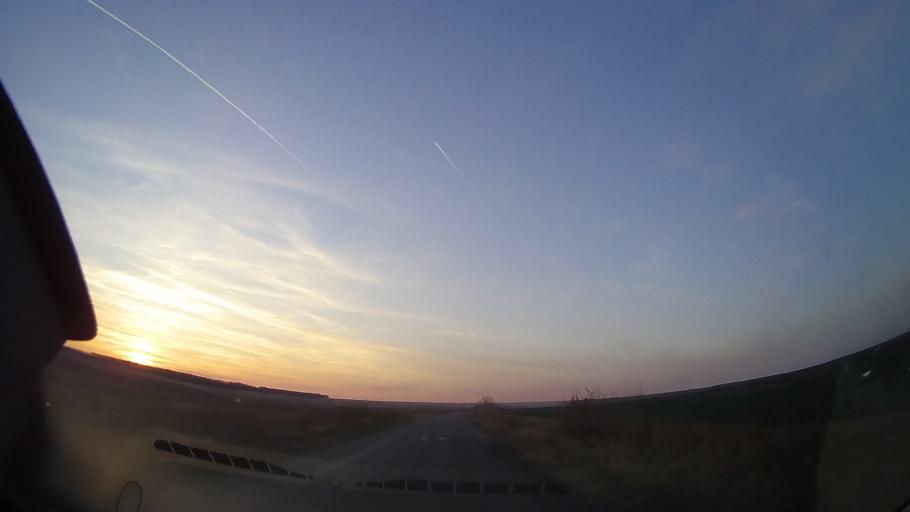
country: RO
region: Constanta
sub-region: Comuna Mereni
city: Mereni
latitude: 44.0158
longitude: 28.3104
